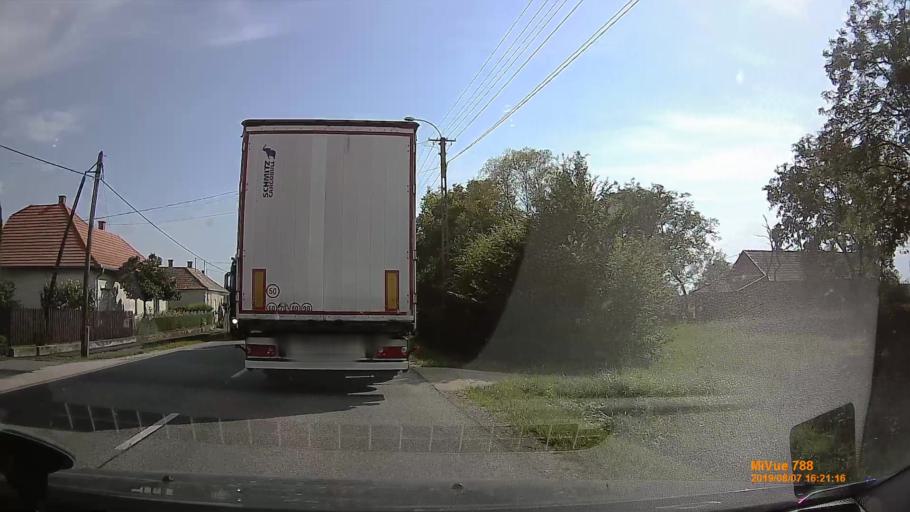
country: HU
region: Zala
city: Zalalovo
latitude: 46.7644
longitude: 16.5651
